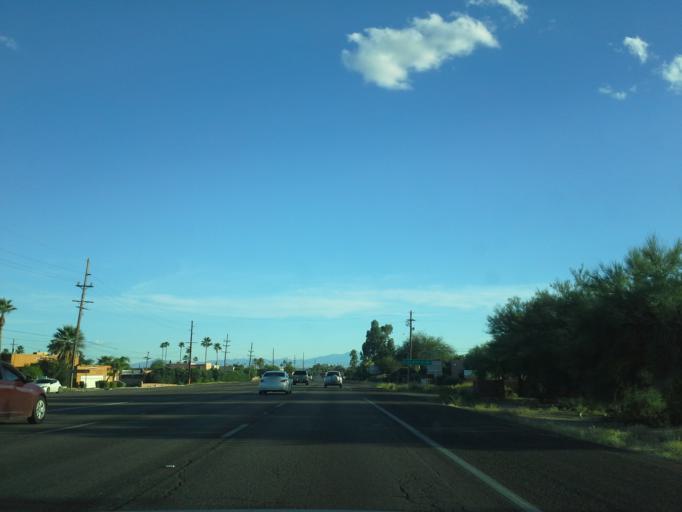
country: US
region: Arizona
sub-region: Pima County
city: Casas Adobes
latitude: 32.3278
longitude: -110.9762
